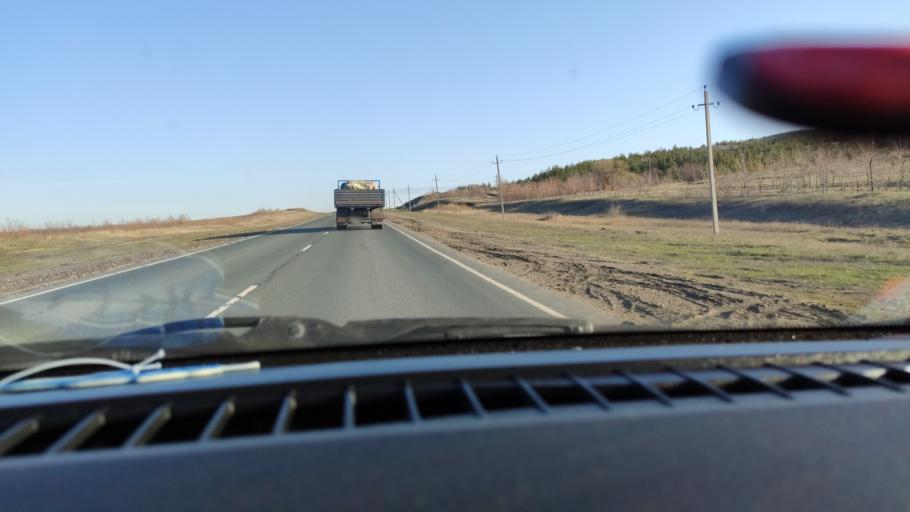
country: RU
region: Saratov
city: Alekseyevka
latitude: 52.2979
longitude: 47.9279
